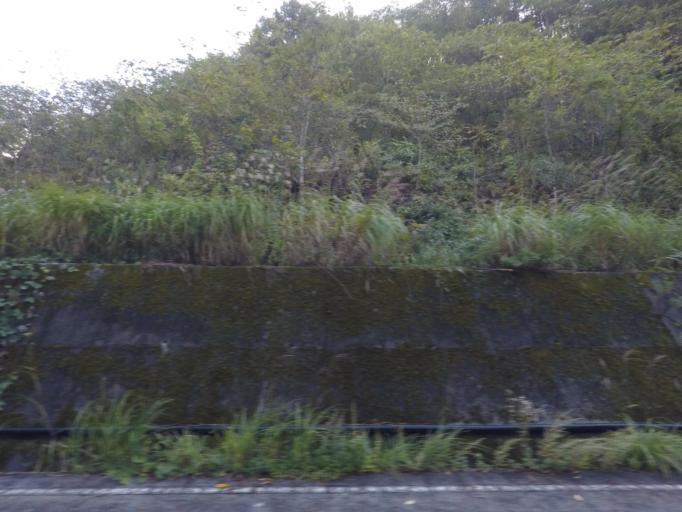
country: JP
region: Nagano
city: Tatsuno
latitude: 35.9715
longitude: 137.7748
